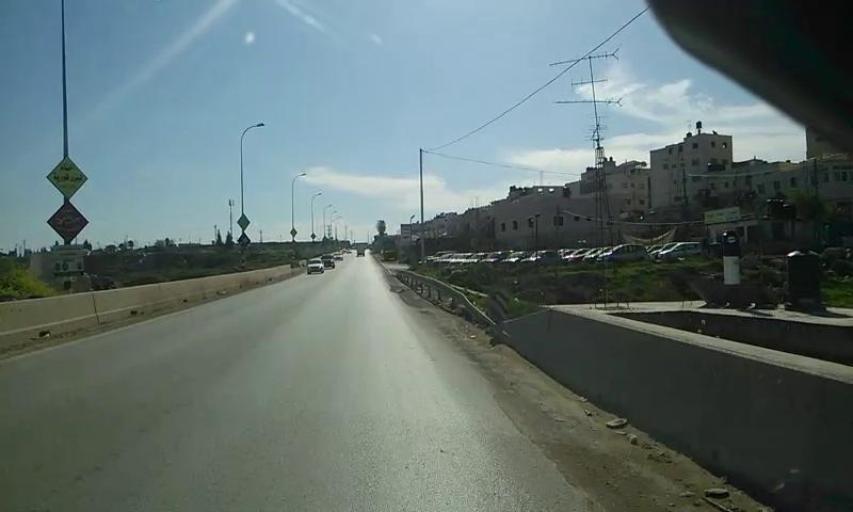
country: PS
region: West Bank
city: Ar Ram wa Dahiyat al Barid
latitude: 31.8574
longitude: 35.2378
